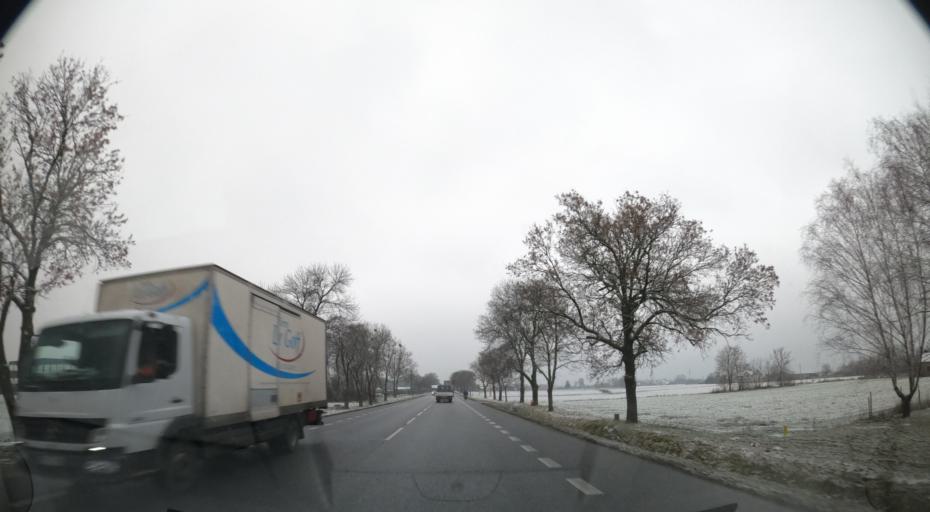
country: PL
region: Masovian Voivodeship
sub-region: Powiat warszawski zachodni
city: Bieniewice
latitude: 52.2051
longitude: 20.5045
